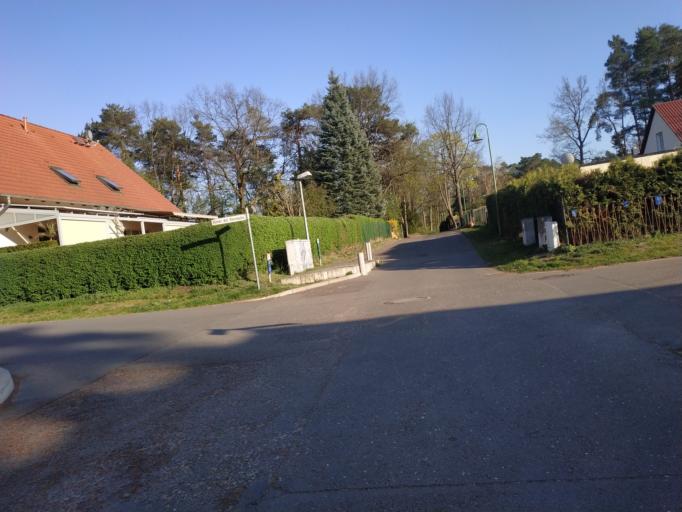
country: DE
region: Brandenburg
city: Petershagen
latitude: 52.5438
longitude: 13.8355
